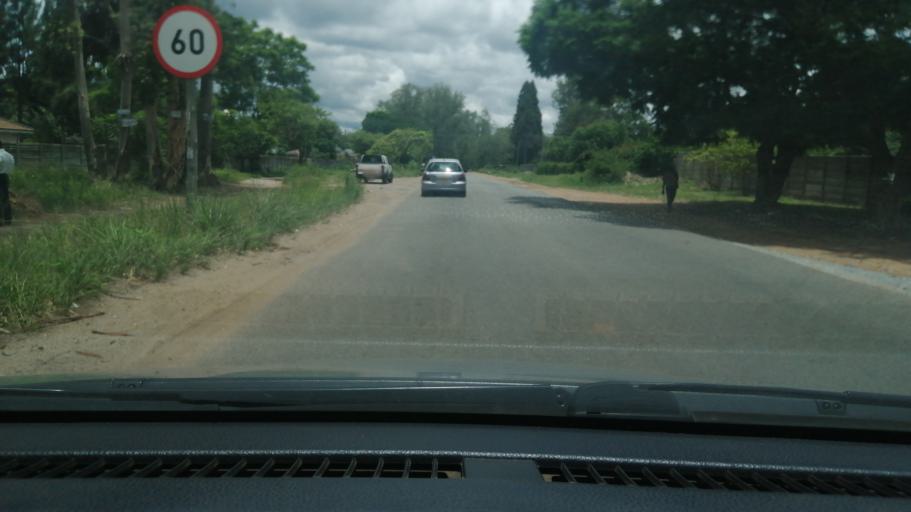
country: ZW
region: Harare
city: Harare
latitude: -17.8834
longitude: 31.0763
